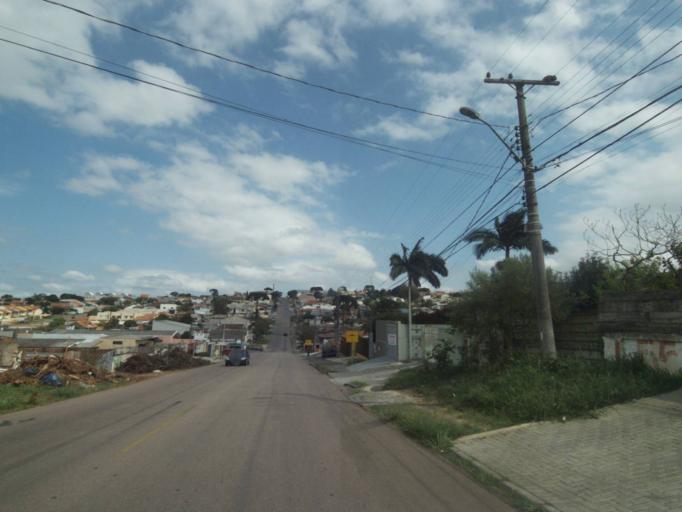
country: BR
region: Parana
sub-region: Pinhais
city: Pinhais
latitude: -25.3968
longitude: -49.2021
